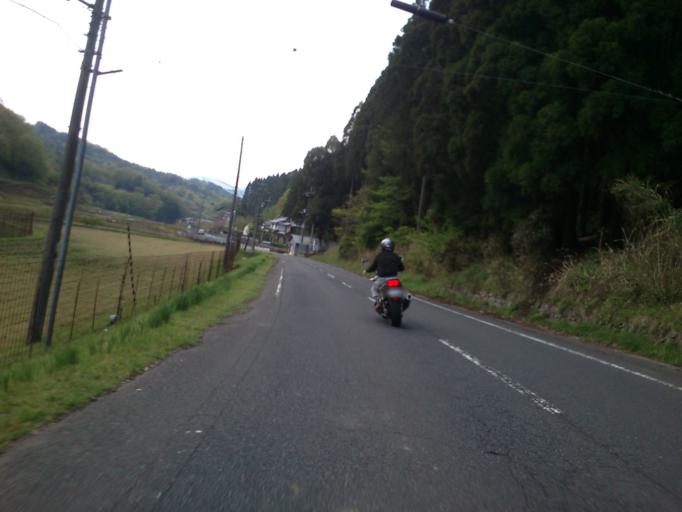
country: JP
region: Kyoto
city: Fukuchiyama
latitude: 35.3149
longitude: 134.9632
